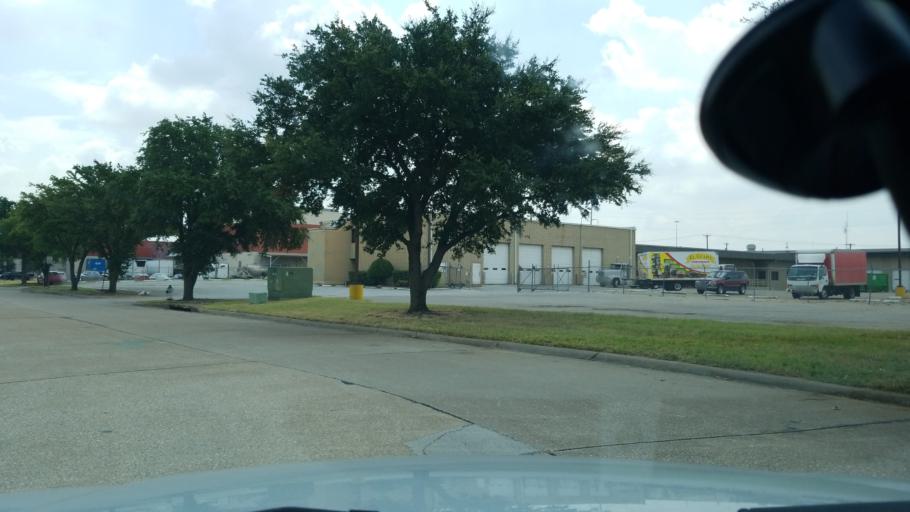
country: US
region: Texas
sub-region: Dallas County
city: Irving
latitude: 32.8384
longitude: -96.8985
